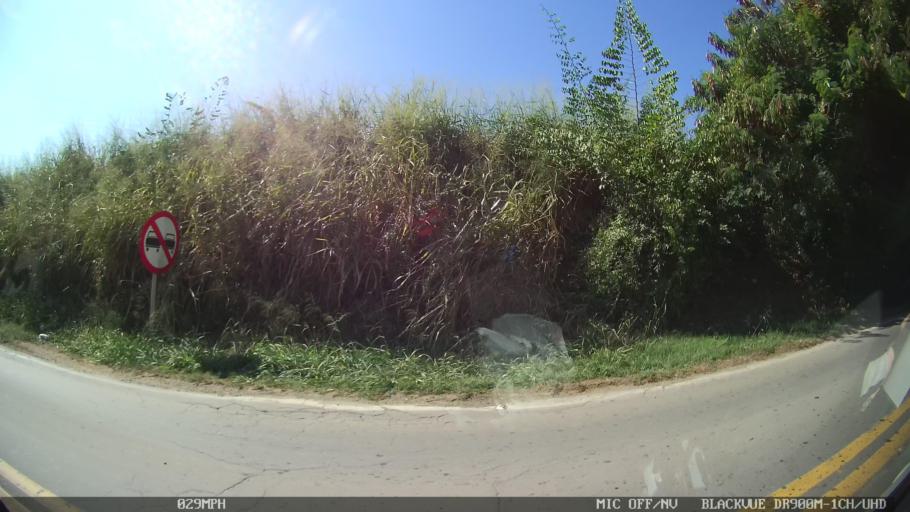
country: BR
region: Sao Paulo
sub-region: Campinas
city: Campinas
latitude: -22.9944
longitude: -47.0857
